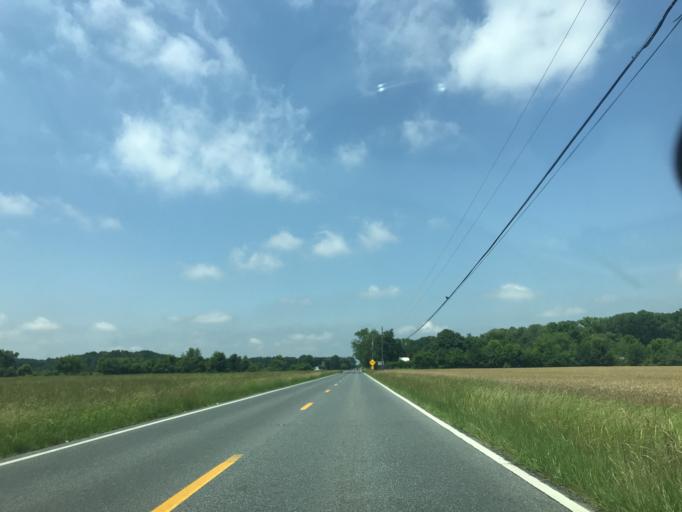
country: US
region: Maryland
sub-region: Dorchester County
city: Hurlock
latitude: 38.5936
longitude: -75.9513
